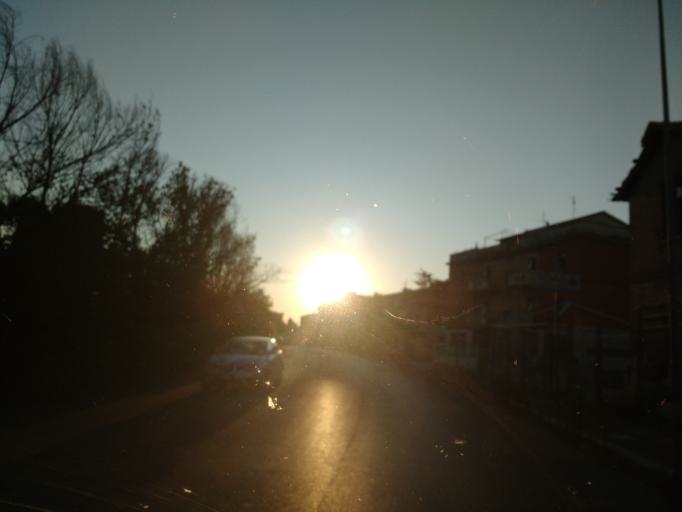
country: IT
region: Latium
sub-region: Citta metropolitana di Roma Capitale
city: Bagni di Tivoli
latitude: 41.9539
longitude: 12.7122
